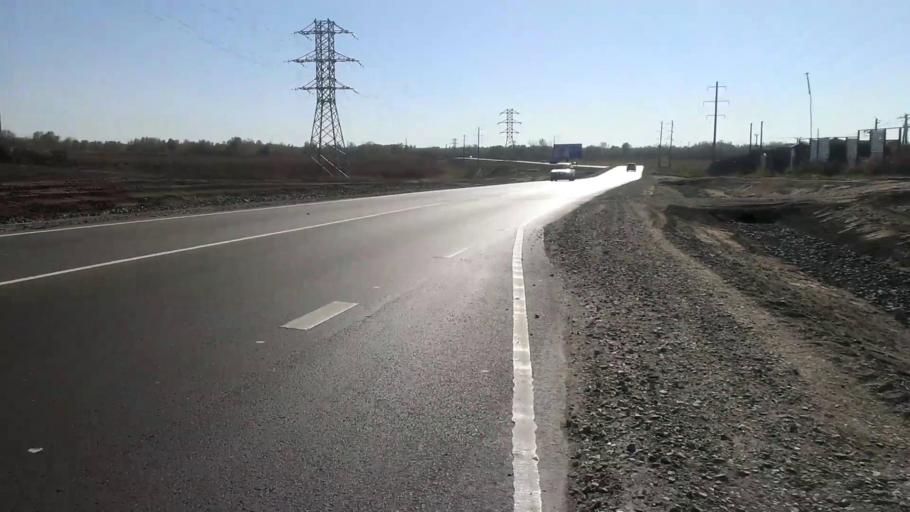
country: RU
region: Altai Krai
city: Sannikovo
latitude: 53.3359
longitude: 83.9385
